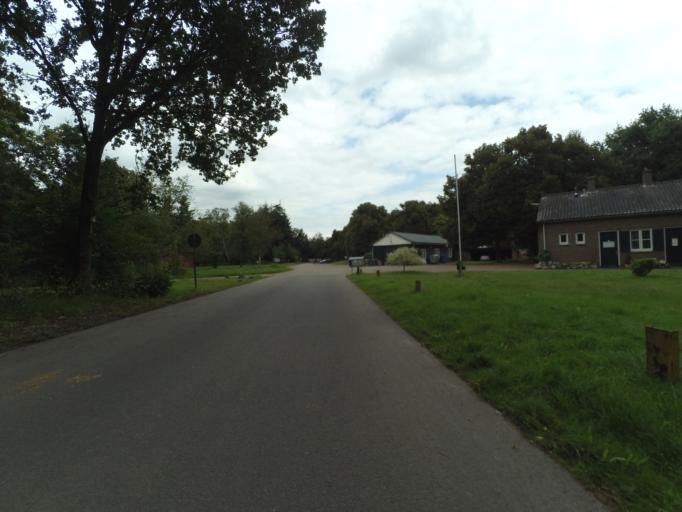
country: NL
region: Utrecht
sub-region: Gemeente Amersfoort
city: Amersfoort
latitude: 52.1233
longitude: 5.3623
